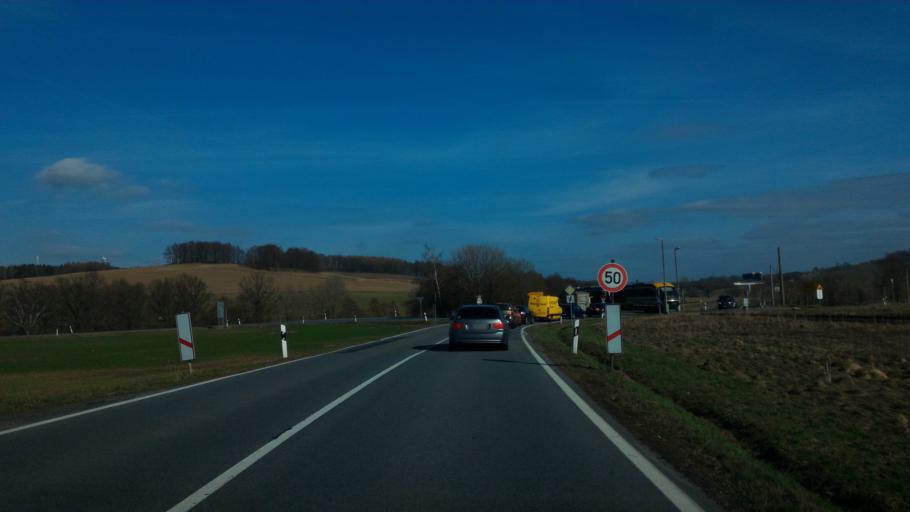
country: DE
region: Saxony
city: Neustadt in Sachsen
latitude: 51.0374
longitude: 14.1591
